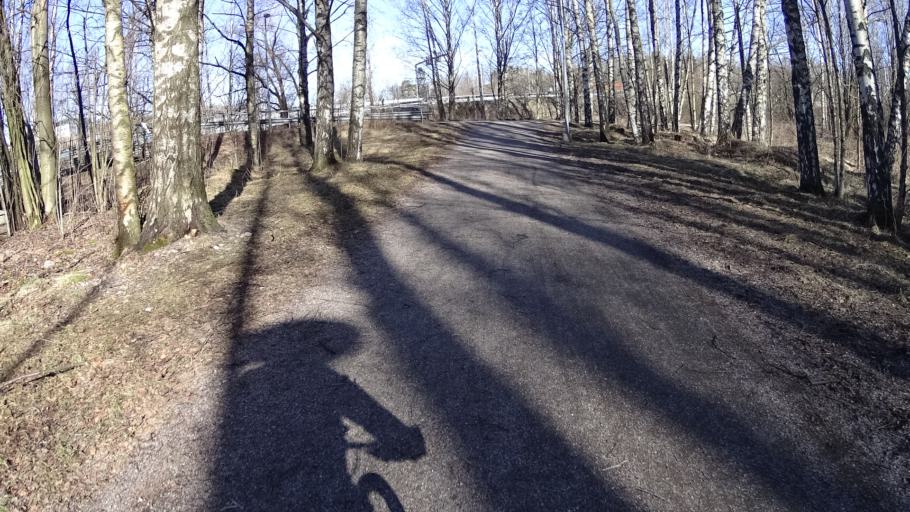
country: FI
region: Uusimaa
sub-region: Helsinki
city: Koukkuniemi
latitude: 60.1641
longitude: 24.7549
